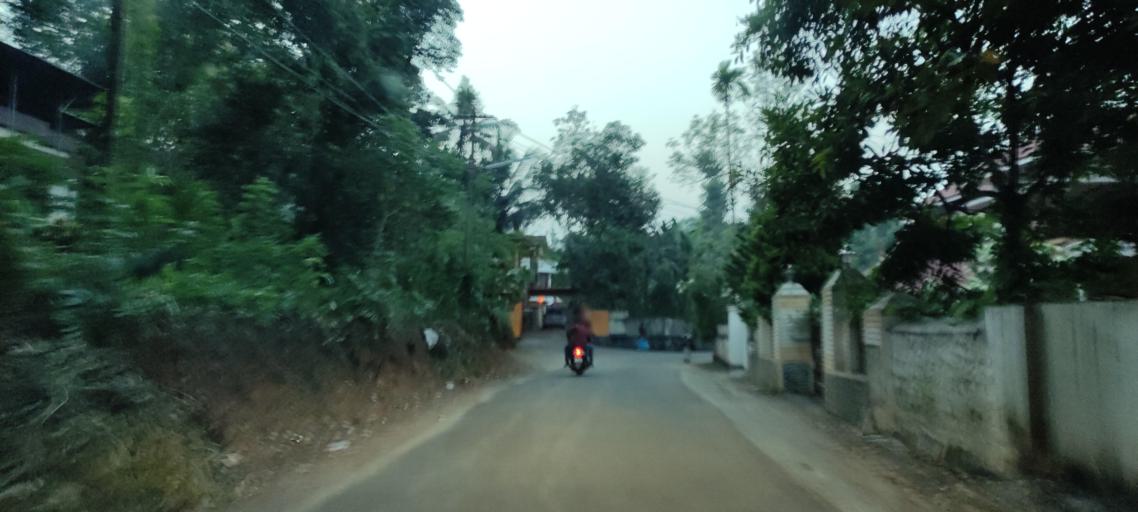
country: IN
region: Kerala
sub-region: Pattanamtitta
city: Adur
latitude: 9.1571
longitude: 76.7347
